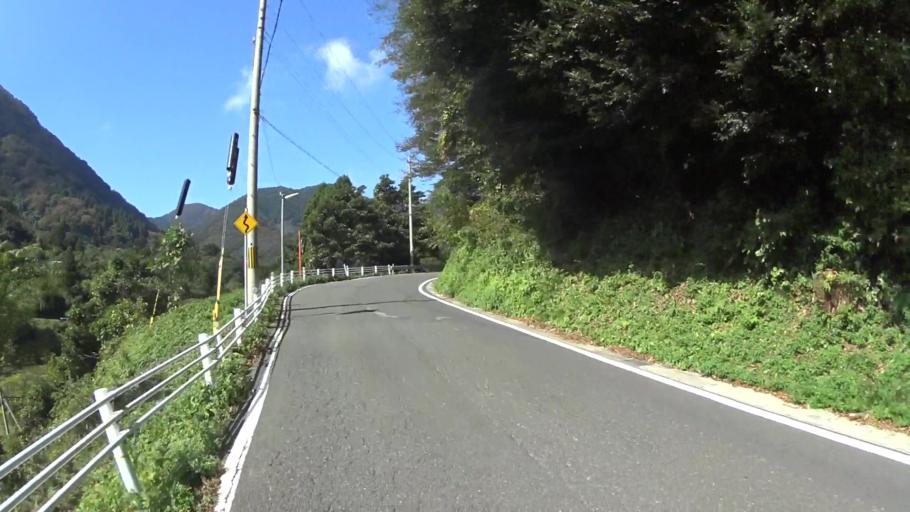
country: JP
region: Kyoto
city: Miyazu
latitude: 35.7417
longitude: 135.2453
